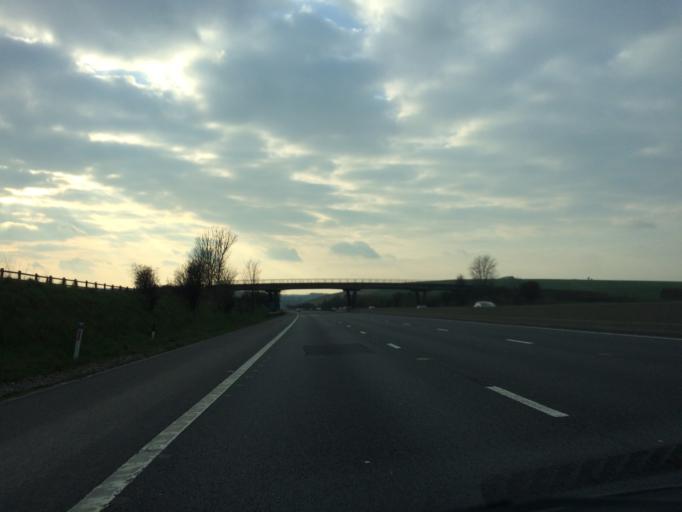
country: GB
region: England
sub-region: Wiltshire
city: Aldbourne
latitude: 51.5124
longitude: -1.6271
